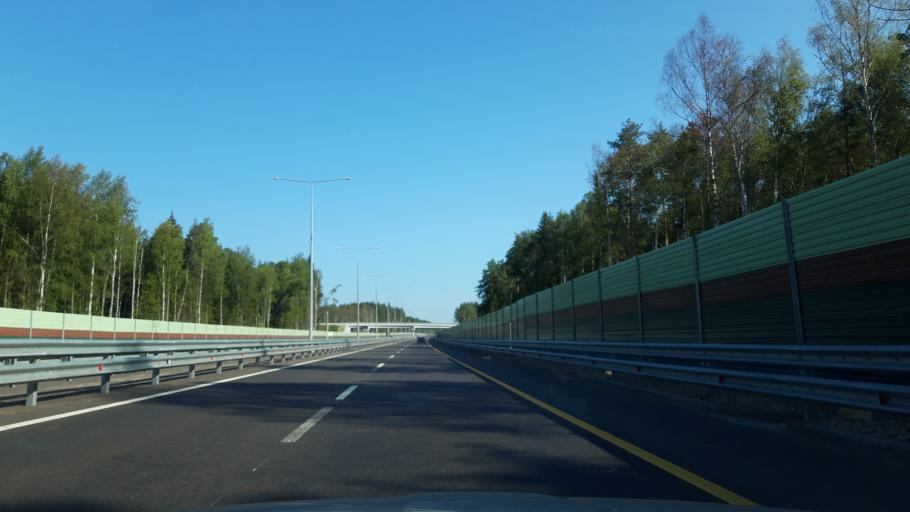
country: RU
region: Moskovskaya
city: Reshetnikovo
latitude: 56.4425
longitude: 36.5424
